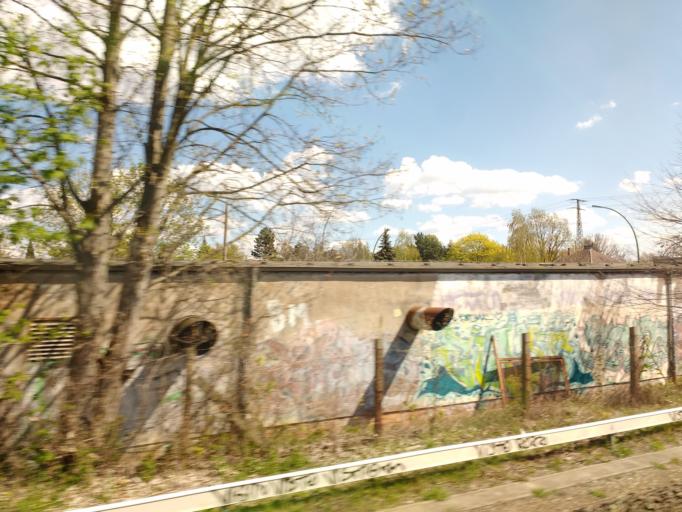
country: DE
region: Berlin
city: Adlershof
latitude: 52.4242
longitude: 13.5571
